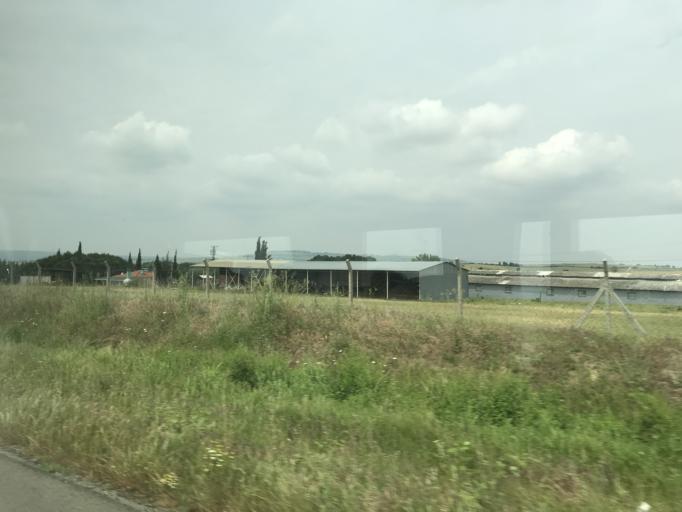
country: TR
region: Tekirdag
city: Inecik
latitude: 40.9330
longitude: 27.2494
